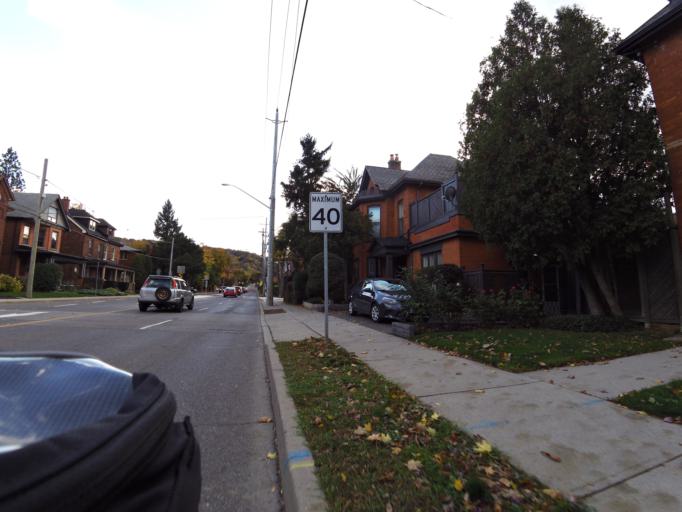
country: CA
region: Ontario
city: Hamilton
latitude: 43.2512
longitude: -79.8823
